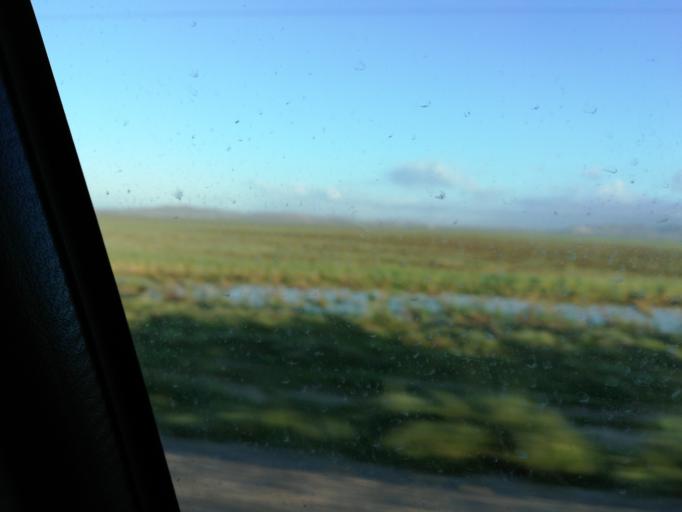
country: TN
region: Susah
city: Harqalah
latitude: 36.0727
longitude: 10.3440
